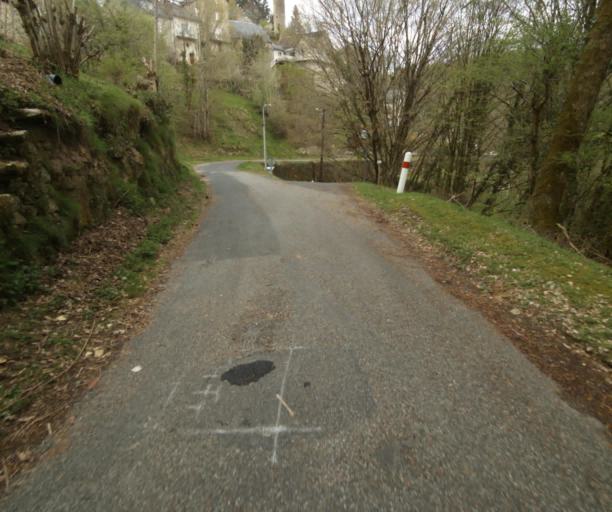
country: FR
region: Limousin
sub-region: Departement de la Correze
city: Argentat
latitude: 45.1946
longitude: 1.9743
